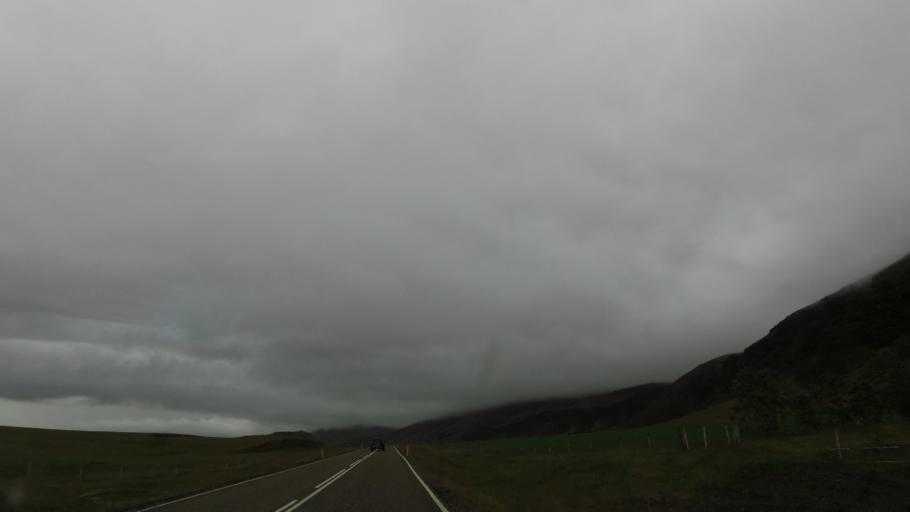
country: IS
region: East
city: Hoefn
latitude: 64.3463
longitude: -15.2473
